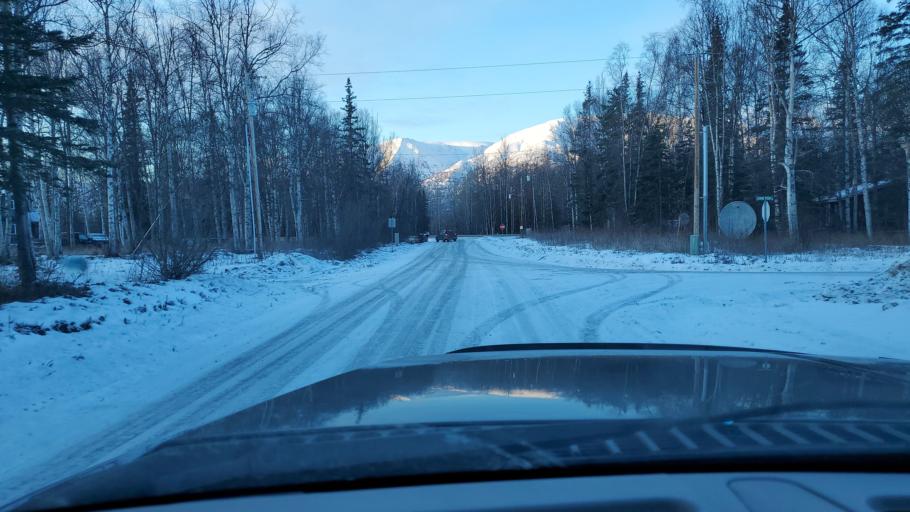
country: US
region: Alaska
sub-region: Matanuska-Susitna Borough
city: Lakes
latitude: 61.6678
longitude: -149.2946
